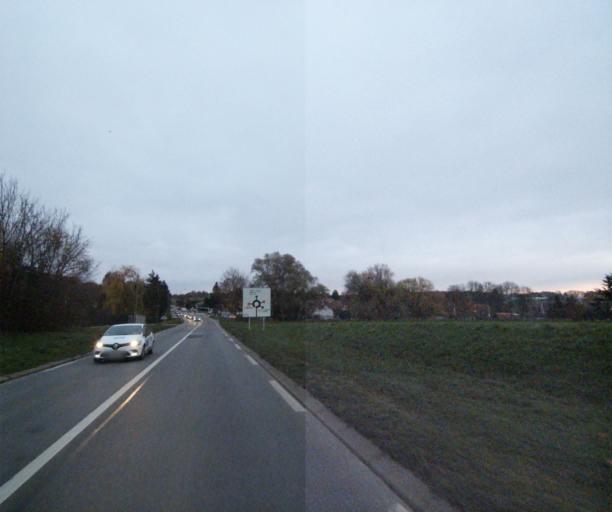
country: FR
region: Ile-de-France
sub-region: Departement des Yvelines
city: Villennes-sur-Seine
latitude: 48.9389
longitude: 1.9770
